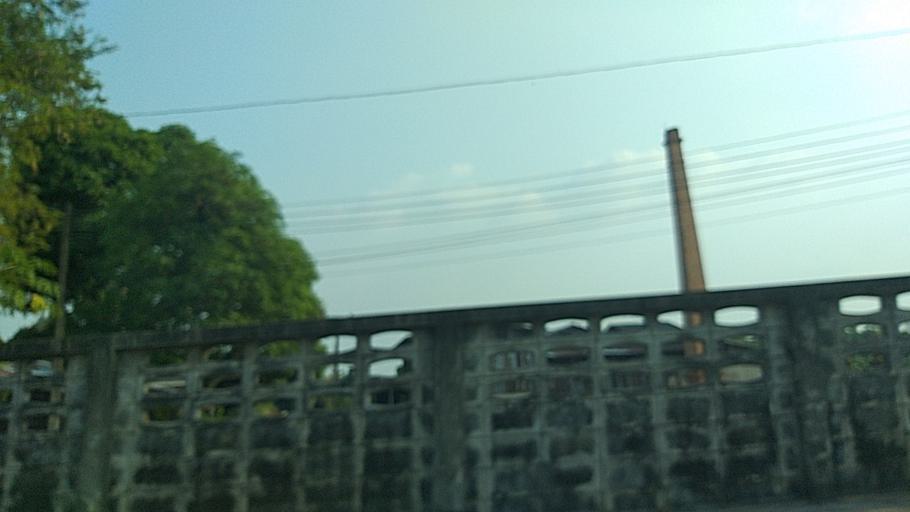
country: TH
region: Nakhon Nayok
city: Nakhon Nayok
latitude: 14.2019
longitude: 101.2019
